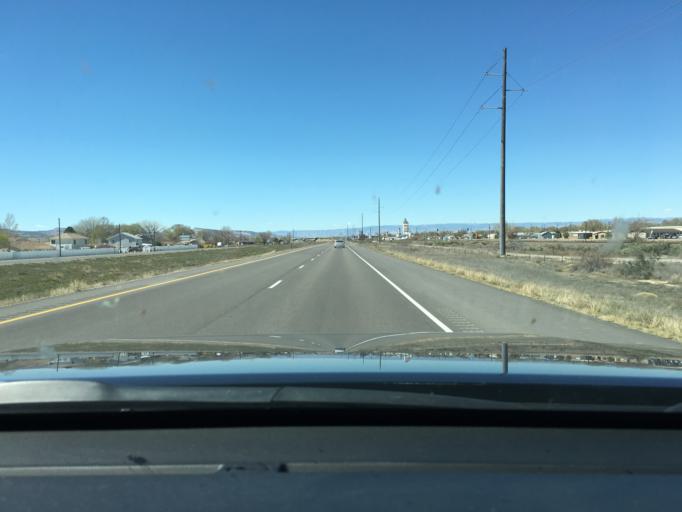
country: US
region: Colorado
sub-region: Mesa County
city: Fruita
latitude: 39.1489
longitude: -108.7226
